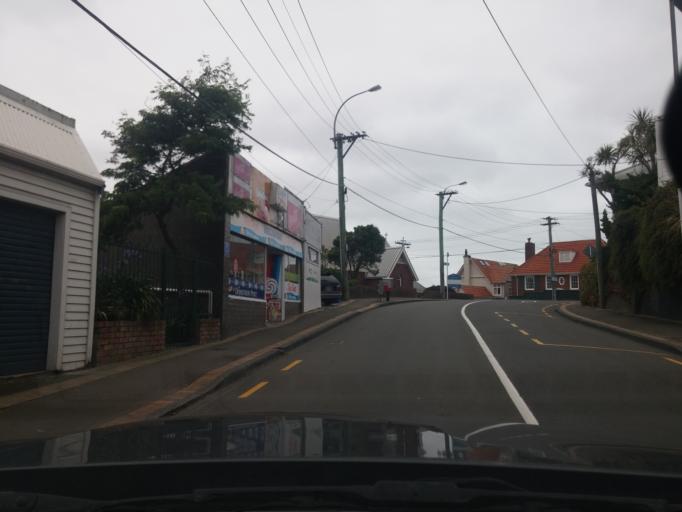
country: NZ
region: Wellington
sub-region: Wellington City
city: Kelburn
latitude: -41.2618
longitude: 174.7750
